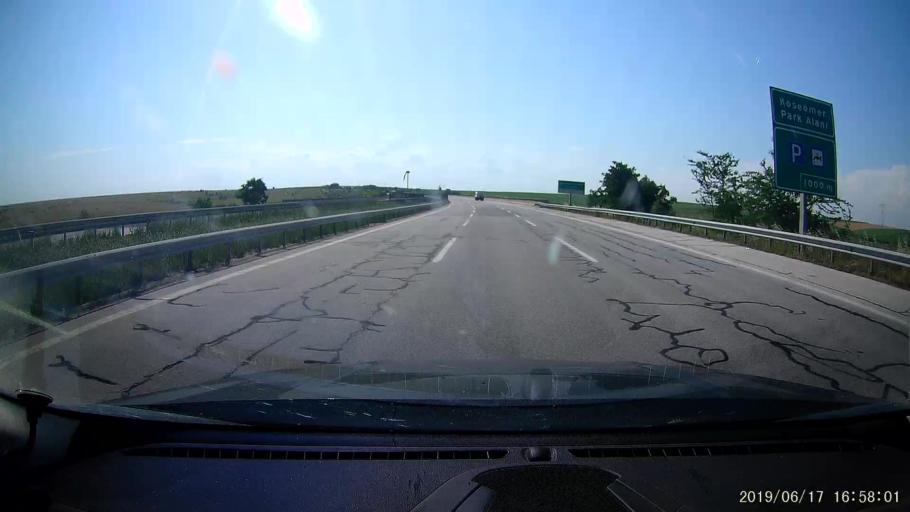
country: TR
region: Edirne
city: Haskoy
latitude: 41.6092
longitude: 26.9005
